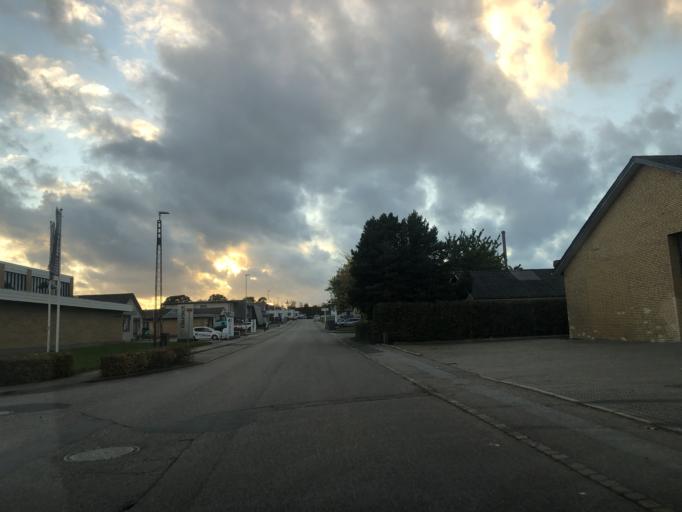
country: DK
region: South Denmark
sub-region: Sonderborg Kommune
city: Sonderborg
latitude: 54.9187
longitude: 9.8144
